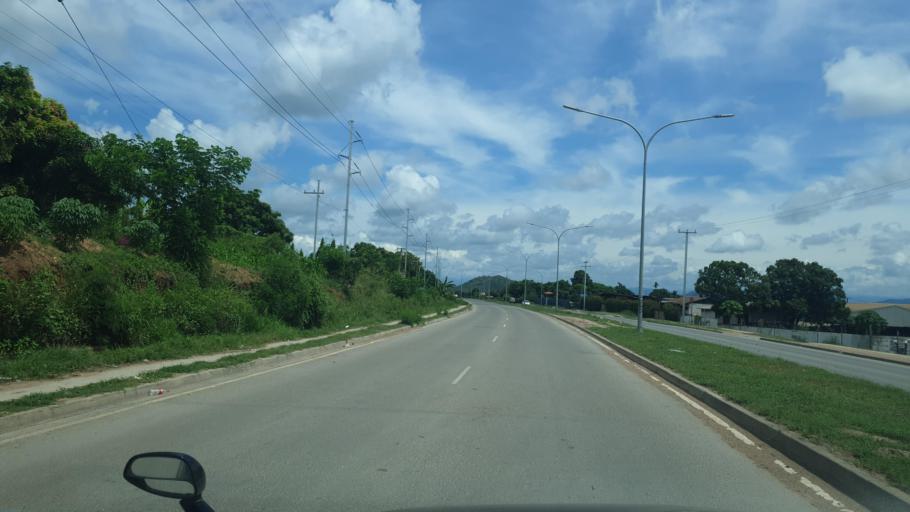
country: PG
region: National Capital
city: Port Moresby
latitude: -9.3864
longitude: 147.1547
